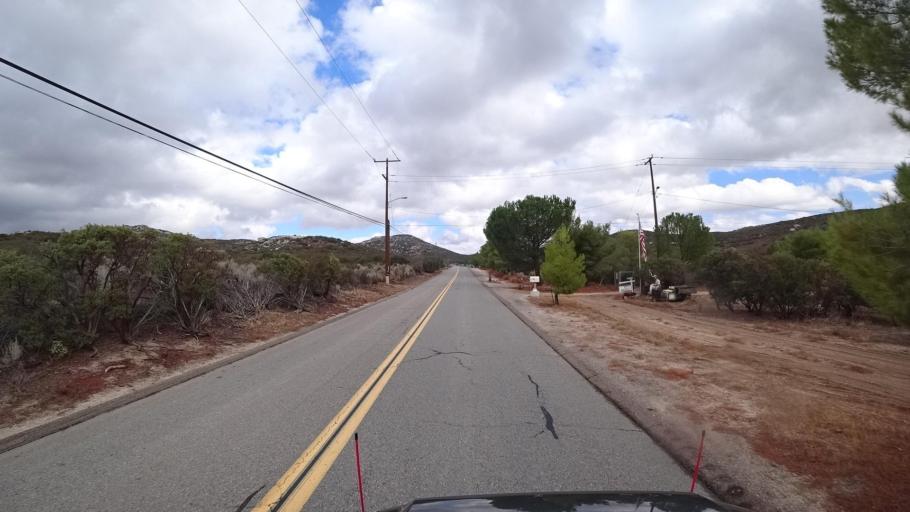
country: US
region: California
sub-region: San Diego County
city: Campo
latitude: 32.6581
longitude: -116.4258
